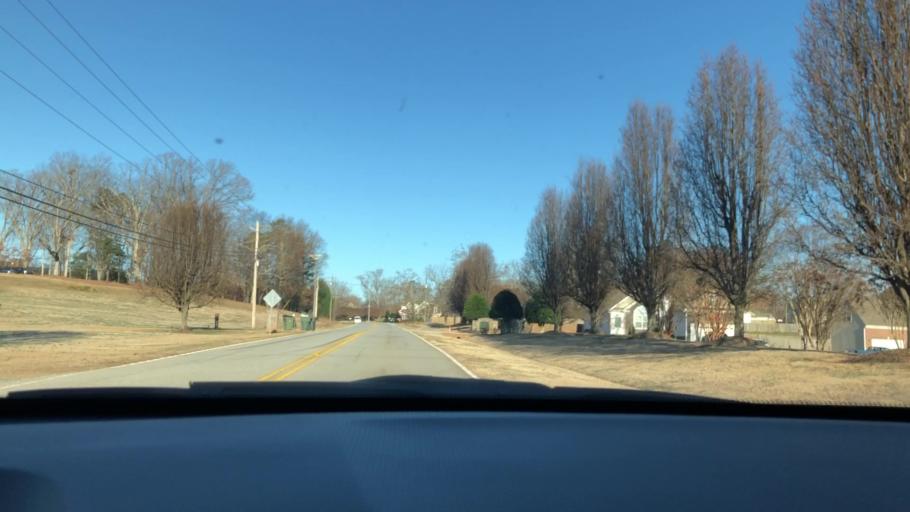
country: US
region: South Carolina
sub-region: Greenville County
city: Five Forks
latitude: 34.8265
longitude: -82.2172
